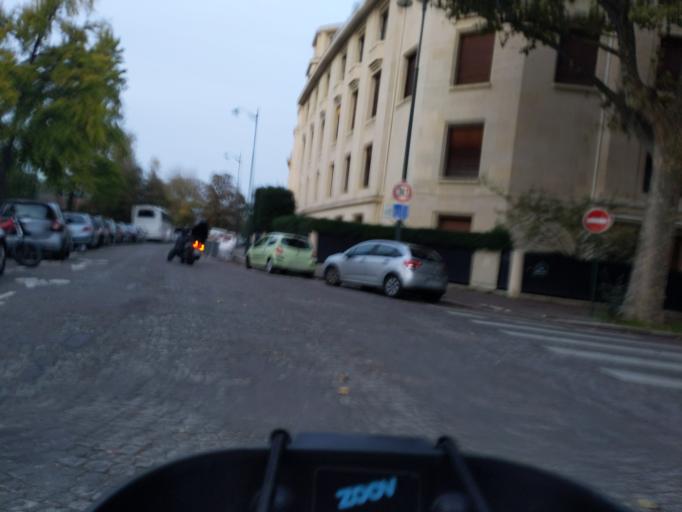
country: FR
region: Ile-de-France
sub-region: Departement des Hauts-de-Seine
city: Neuilly-sur-Seine
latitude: 48.8612
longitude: 2.2659
